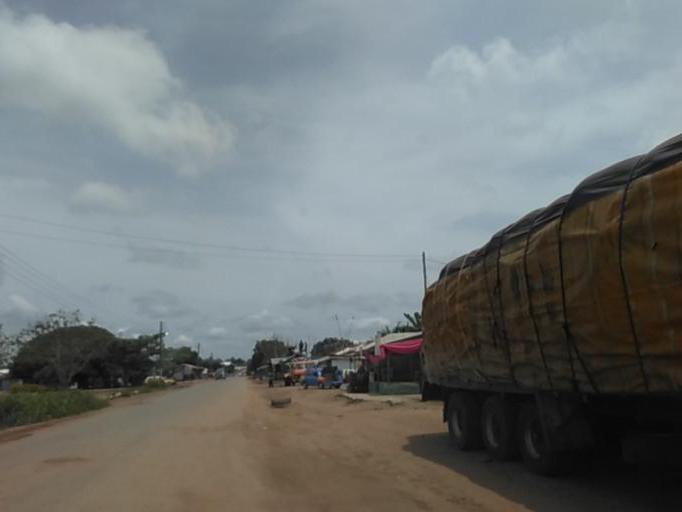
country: GH
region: Ashanti
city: Mamponteng
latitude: 6.8360
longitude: -1.5116
